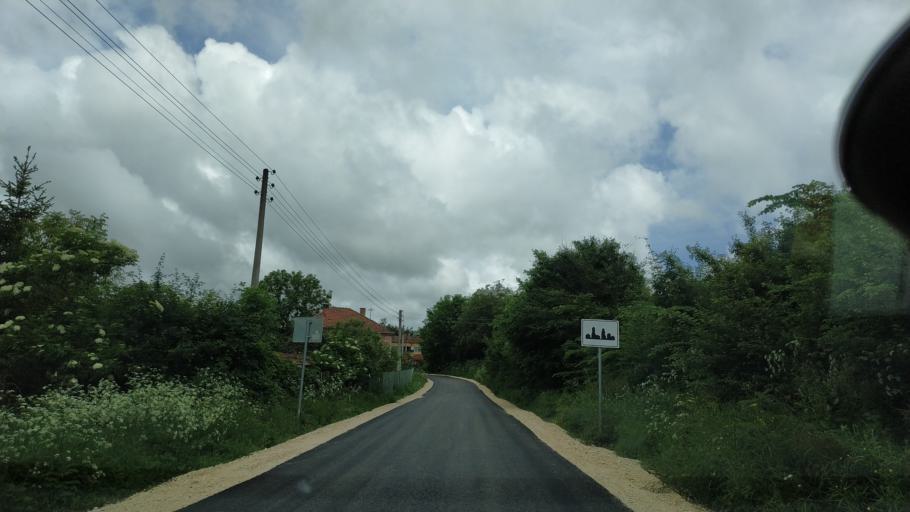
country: RS
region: Central Serbia
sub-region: Zajecarski Okrug
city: Soko Banja
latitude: 43.6709
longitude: 21.9132
